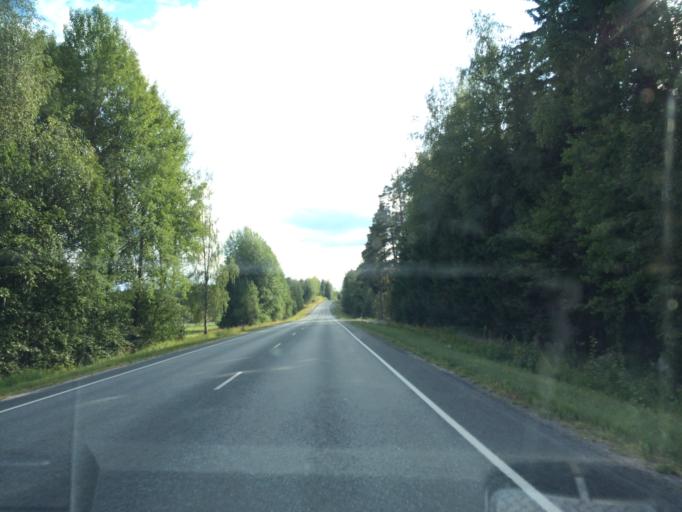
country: FI
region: Haeme
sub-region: Haemeenlinna
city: Haemeenlinna
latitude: 60.9439
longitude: 24.3909
